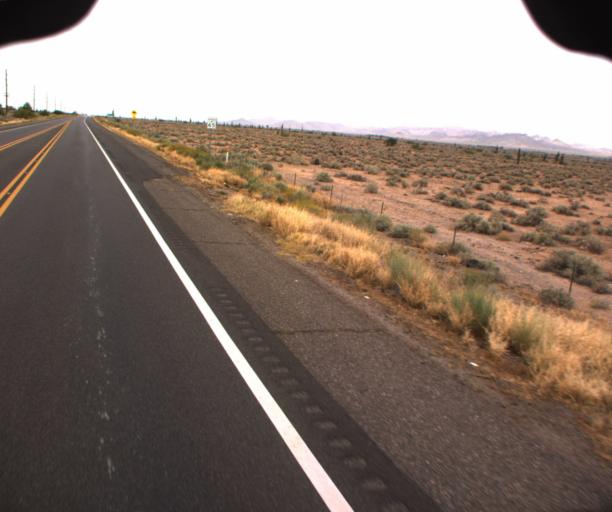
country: US
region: Arizona
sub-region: Pinal County
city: Blackwater
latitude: 33.0218
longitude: -111.6364
